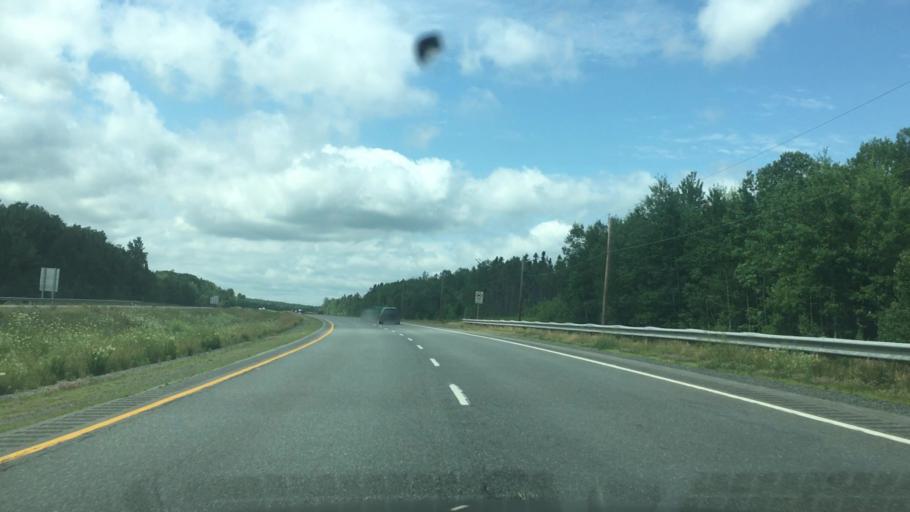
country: CA
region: Nova Scotia
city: Oxford
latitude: 45.7228
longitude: -63.8979
